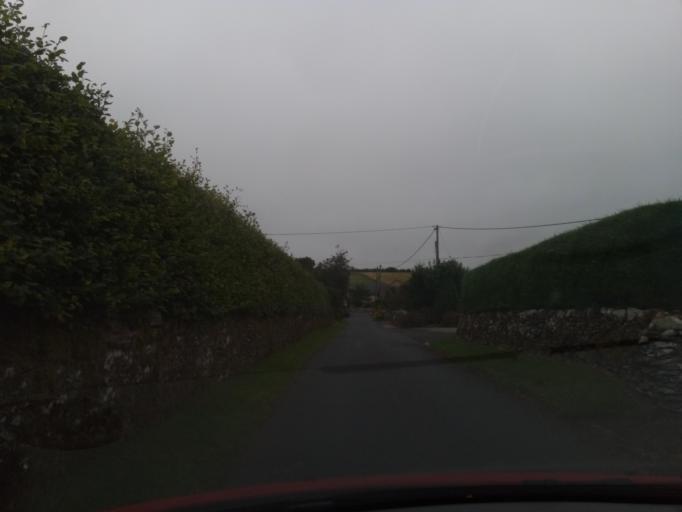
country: GB
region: Scotland
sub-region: The Scottish Borders
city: Hawick
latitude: 55.4490
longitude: -2.7635
